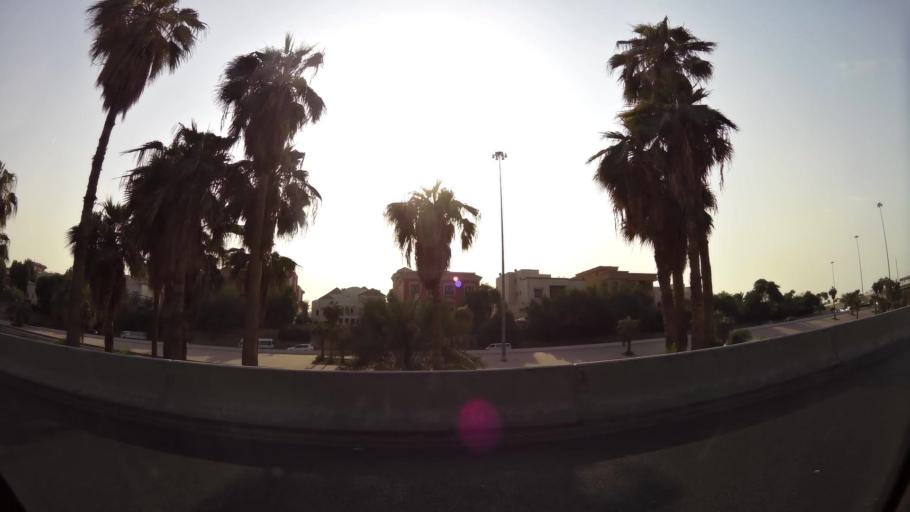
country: KW
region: Muhafazat Hawalli
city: Hawalli
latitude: 29.3218
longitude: 48.0134
